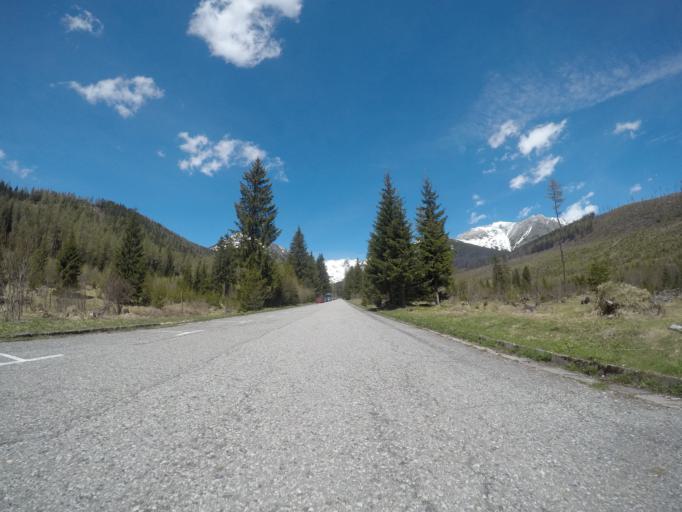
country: SK
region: Presovsky
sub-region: Okres Poprad
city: Strba
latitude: 49.1224
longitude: 20.0748
